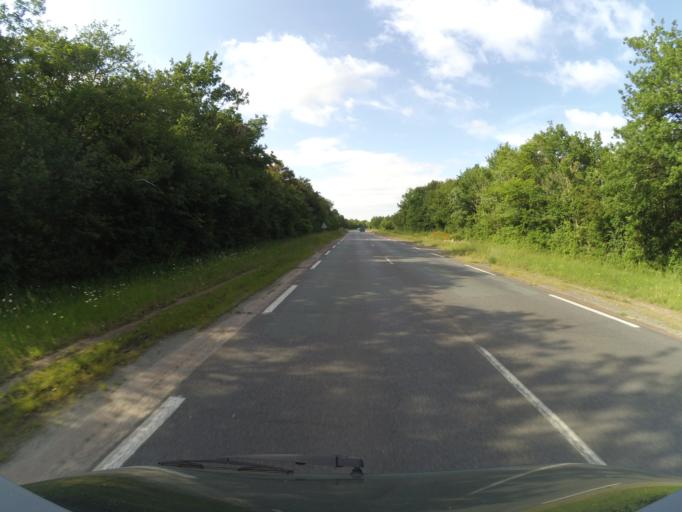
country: FR
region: Poitou-Charentes
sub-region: Departement de la Charente-Maritime
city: Le Gua
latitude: 45.7976
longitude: -0.9361
